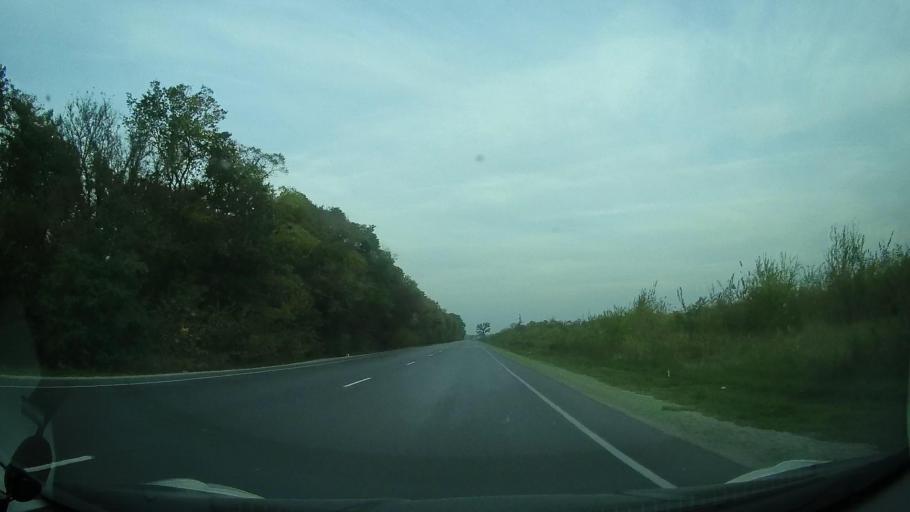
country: RU
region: Rostov
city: Ol'ginskaya
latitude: 47.1312
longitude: 39.9477
